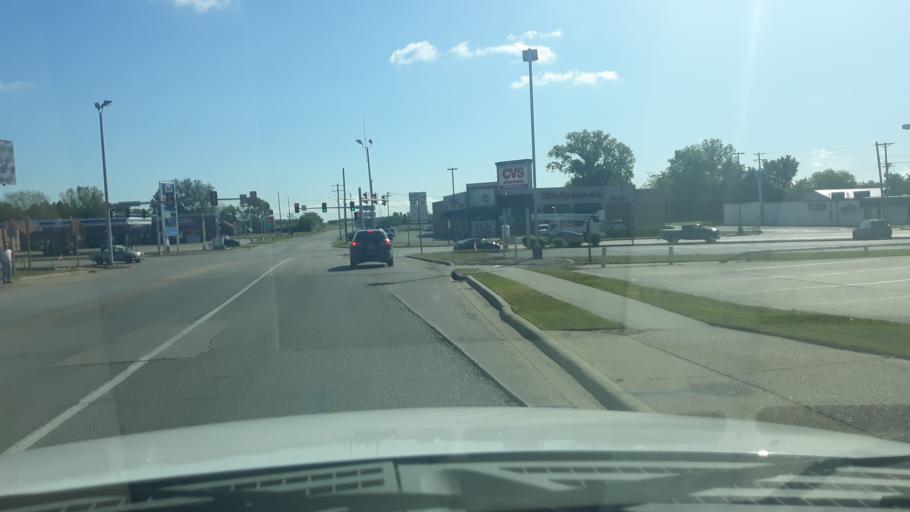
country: US
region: Illinois
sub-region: Saline County
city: Harrisburg
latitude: 37.7383
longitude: -88.5337
